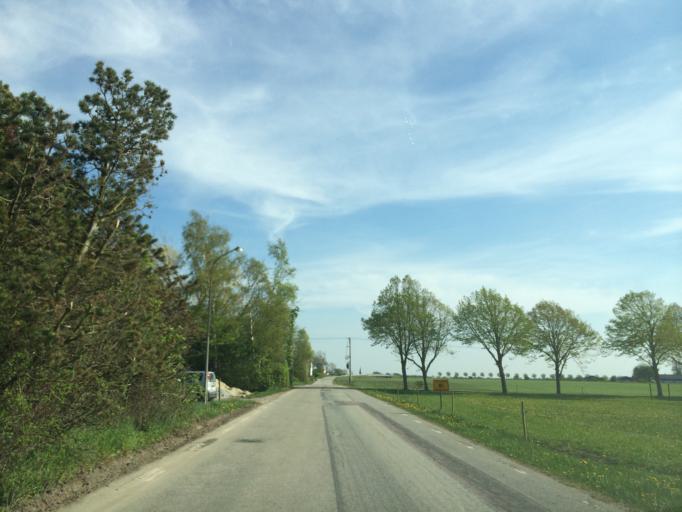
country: SE
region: Skane
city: Bjarred
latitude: 55.7406
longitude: 13.0607
